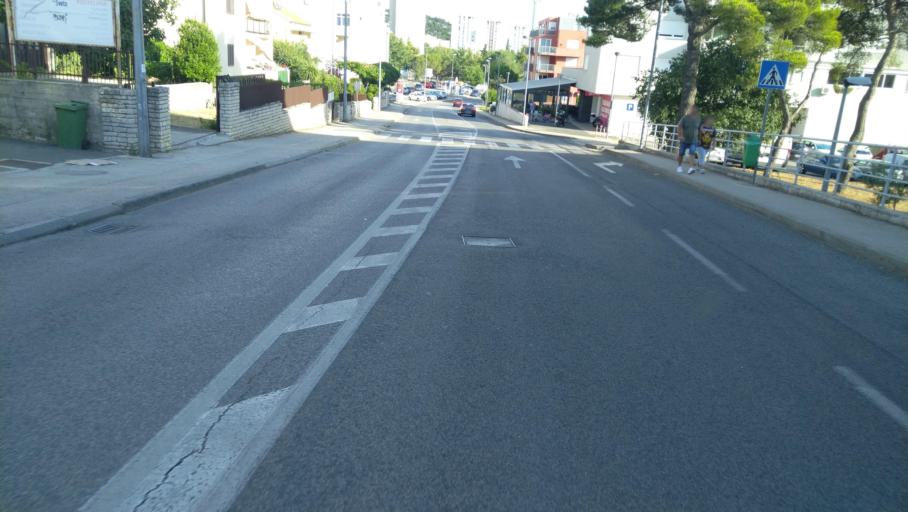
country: HR
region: Sibensko-Kniniska
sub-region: Grad Sibenik
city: Sibenik
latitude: 43.7463
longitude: 15.8956
